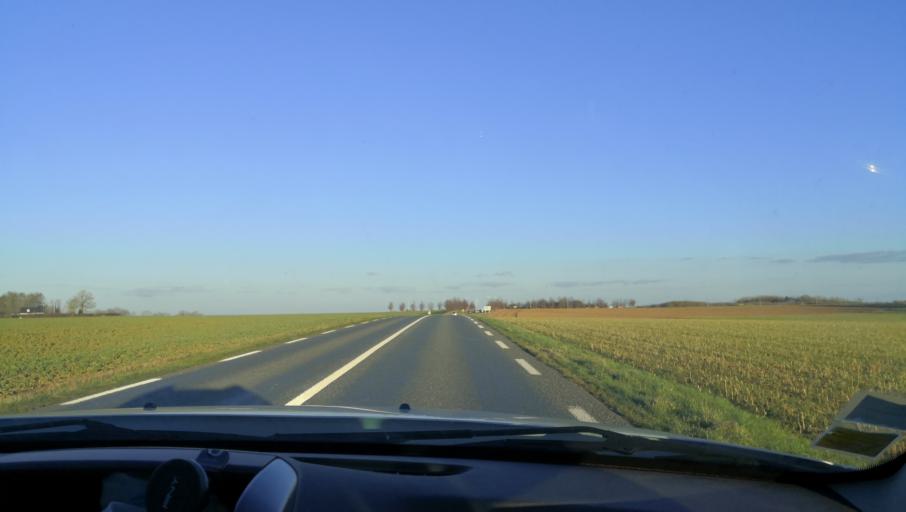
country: FR
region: Haute-Normandie
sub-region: Departement de la Seine-Maritime
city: Buchy
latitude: 49.5936
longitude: 1.4298
